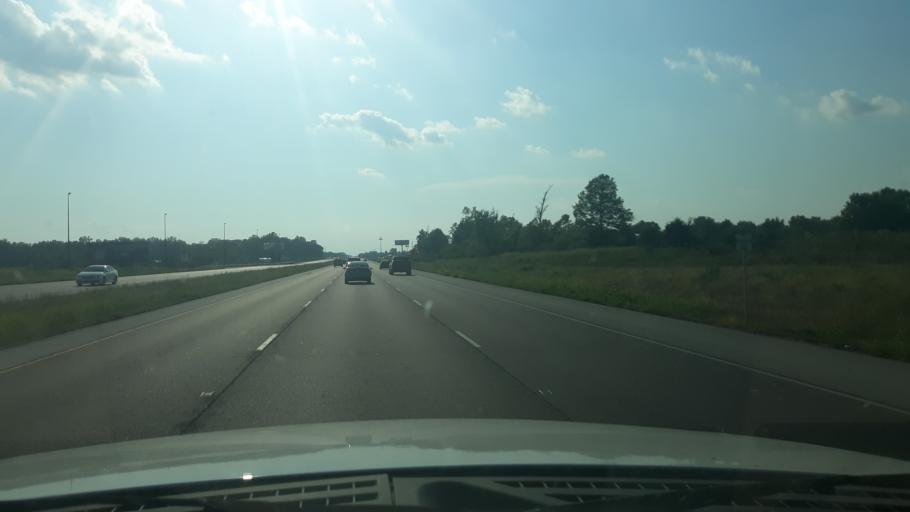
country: US
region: Illinois
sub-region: Williamson County
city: Crainville
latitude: 37.7452
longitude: -89.0602
